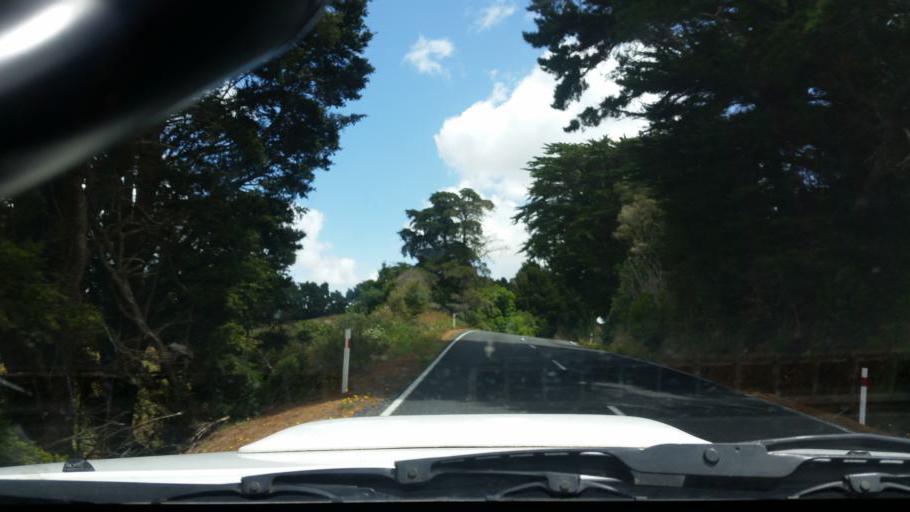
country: NZ
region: Northland
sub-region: Whangarei
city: Ruakaka
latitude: -36.0467
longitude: 174.2775
